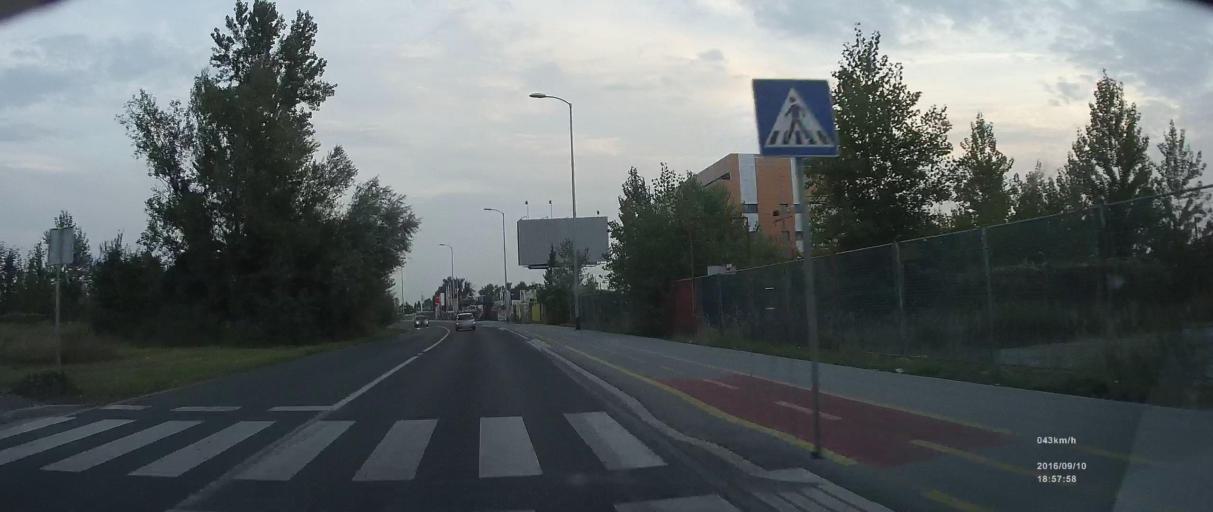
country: HR
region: Grad Zagreb
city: Novi Zagreb
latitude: 45.7632
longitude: 15.9810
